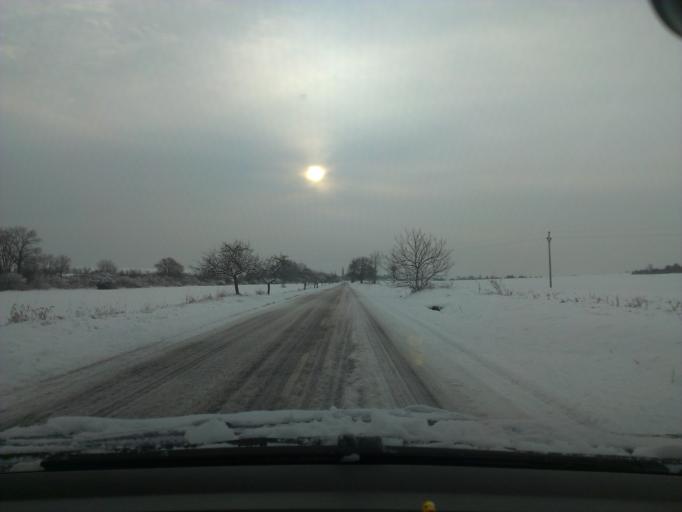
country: SK
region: Trnavsky
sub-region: Okres Trnava
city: Piestany
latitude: 48.5376
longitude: 17.9508
